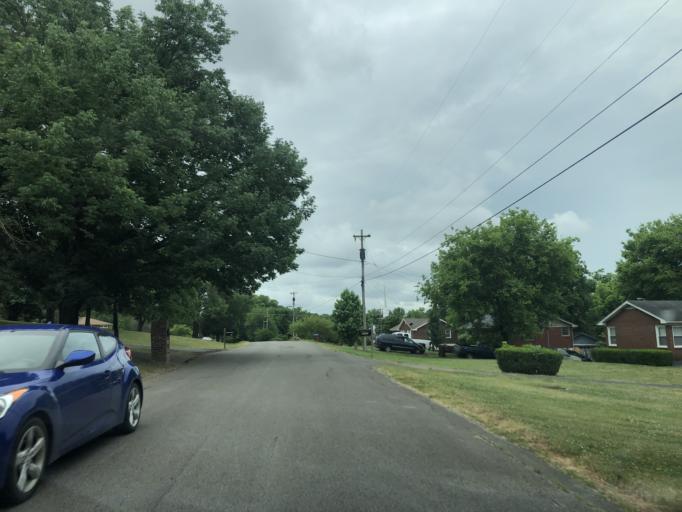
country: US
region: Tennessee
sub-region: Davidson County
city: Goodlettsville
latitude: 36.2654
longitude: -86.7622
